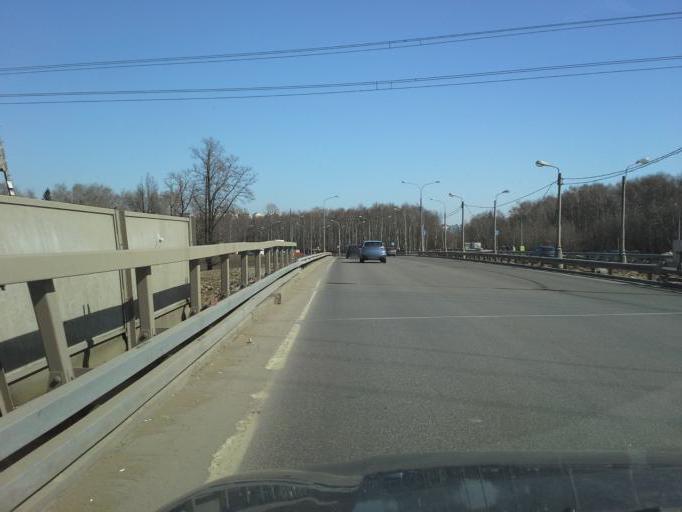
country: RU
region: Moskovskaya
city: Vostryakovo
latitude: 55.6620
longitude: 37.4334
